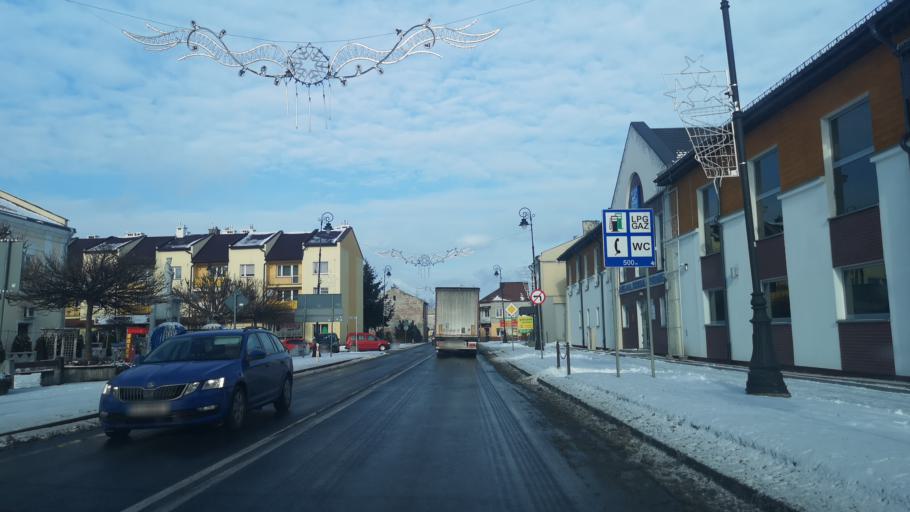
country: PL
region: Subcarpathian Voivodeship
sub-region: Powiat przeworski
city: Sieniawa
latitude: 50.1780
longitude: 22.6096
